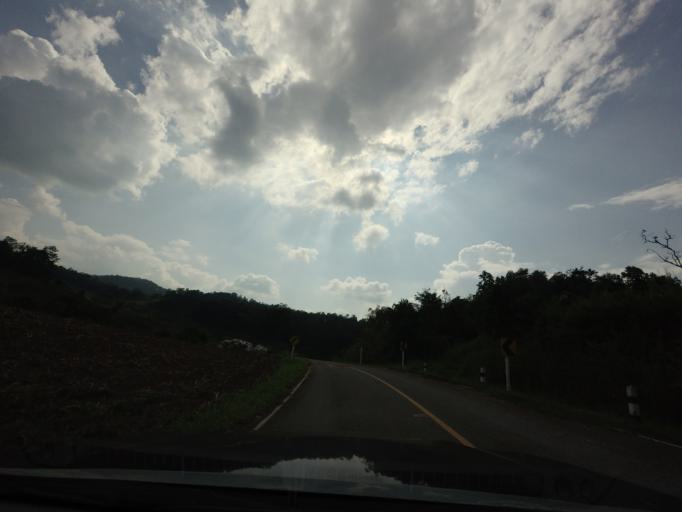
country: TH
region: Uttaradit
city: Ban Khok
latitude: 18.2297
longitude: 101.0165
